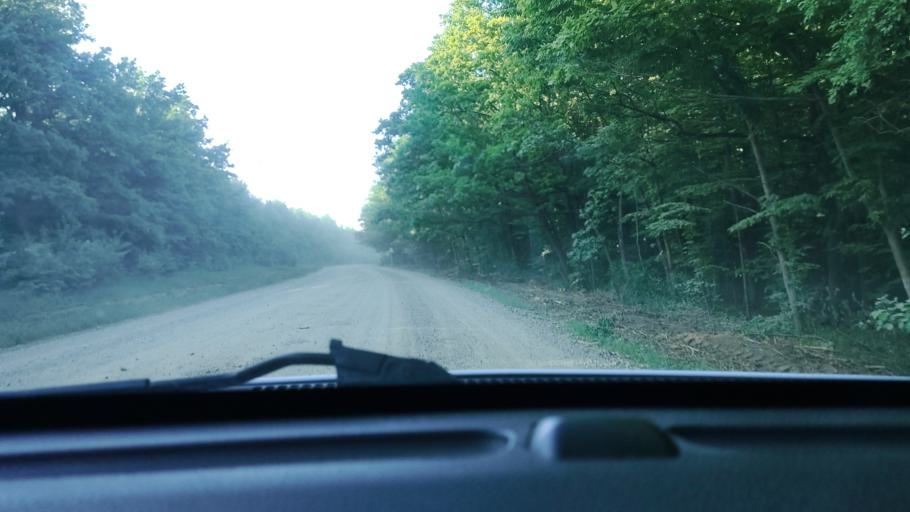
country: RU
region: Krasnodarskiy
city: Goryachiy Klyuch
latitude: 44.7147
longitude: 38.9914
